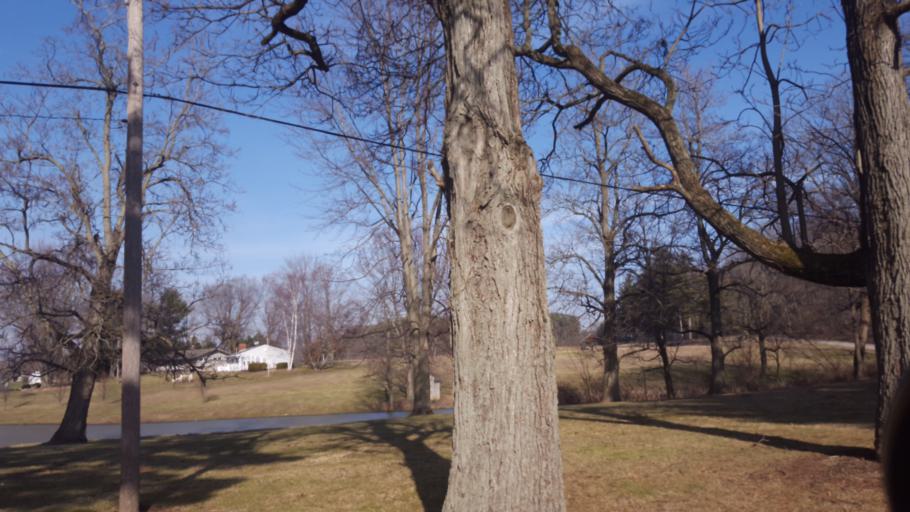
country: US
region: Ohio
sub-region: Crawford County
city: Crestline
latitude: 40.7771
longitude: -82.6796
